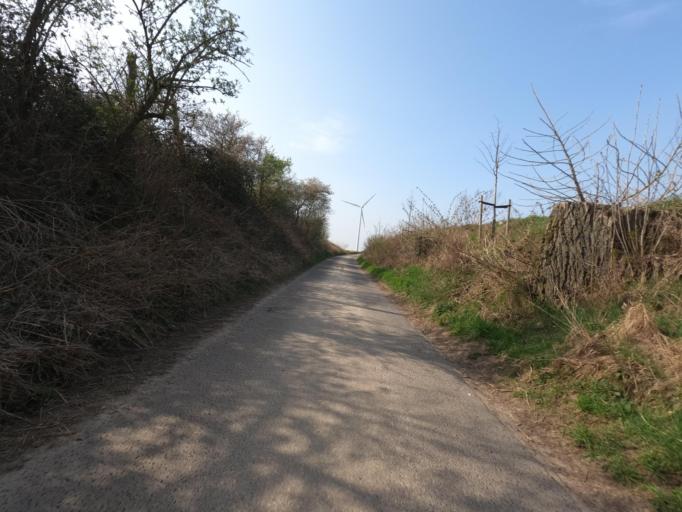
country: DE
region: North Rhine-Westphalia
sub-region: Regierungsbezirk Koln
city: Linnich
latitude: 51.0013
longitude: 6.3117
